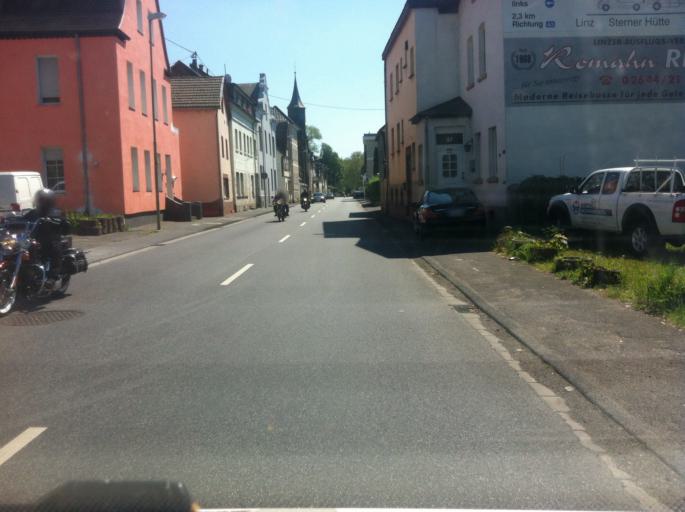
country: DE
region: Rheinland-Pfalz
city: Ockenfels
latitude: 50.5726
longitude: 7.2710
